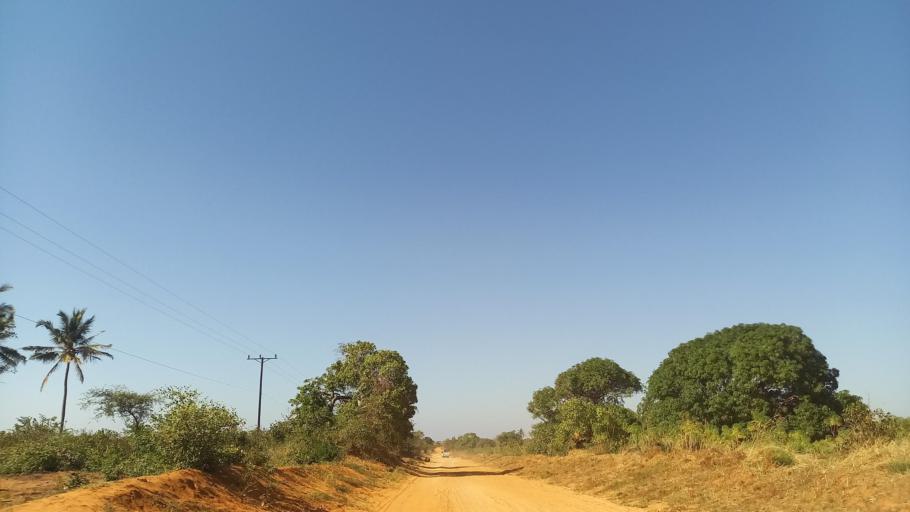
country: MZ
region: Cabo Delgado
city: Pemba
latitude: -13.1531
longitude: 40.5577
